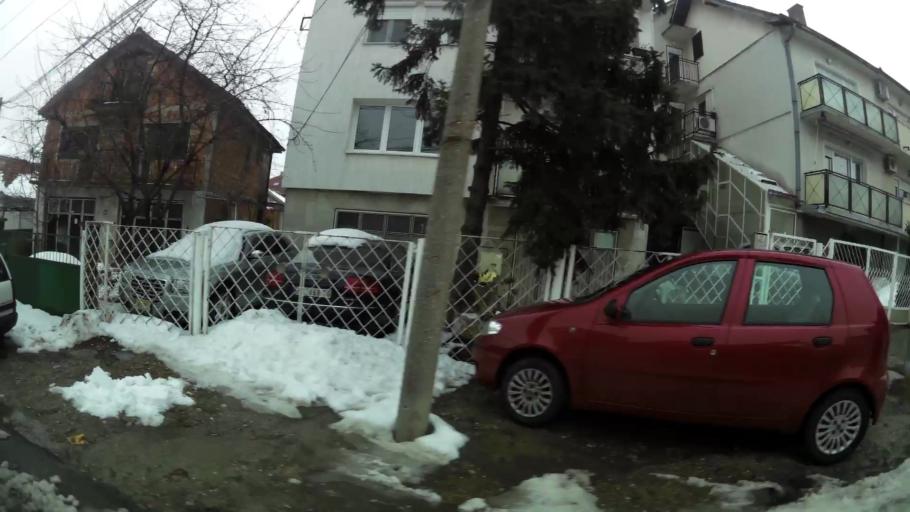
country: RS
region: Central Serbia
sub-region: Belgrade
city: Zvezdara
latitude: 44.7420
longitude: 20.5023
